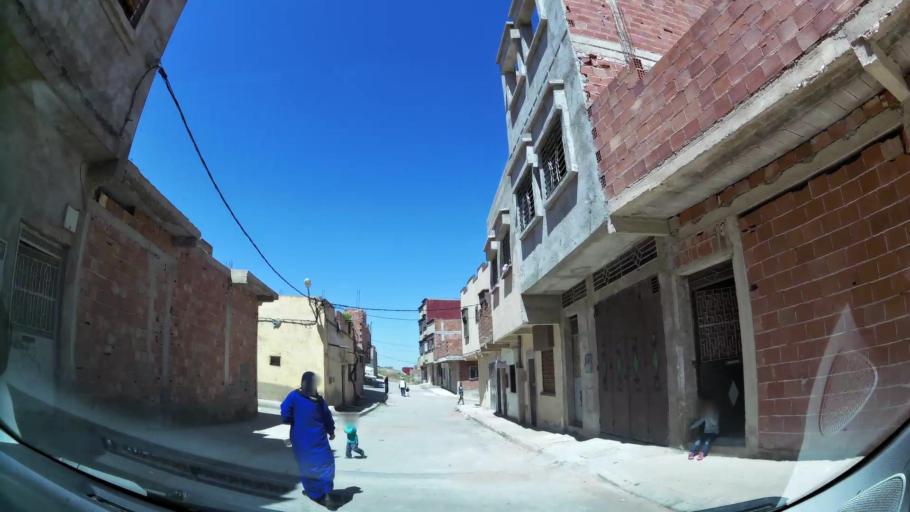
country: MA
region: Oriental
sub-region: Oujda-Angad
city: Oujda
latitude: 34.6482
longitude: -1.8736
